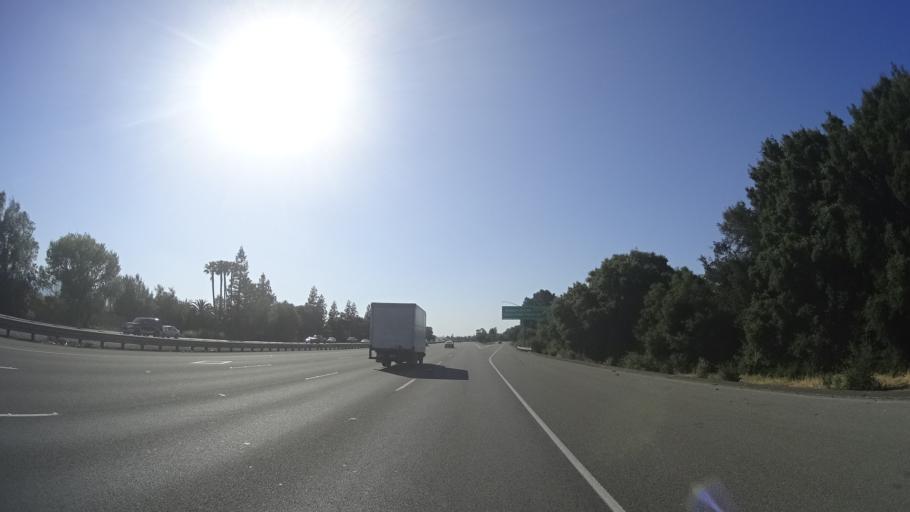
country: US
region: California
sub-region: Santa Clara County
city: Seven Trees
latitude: 37.2527
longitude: -121.7881
